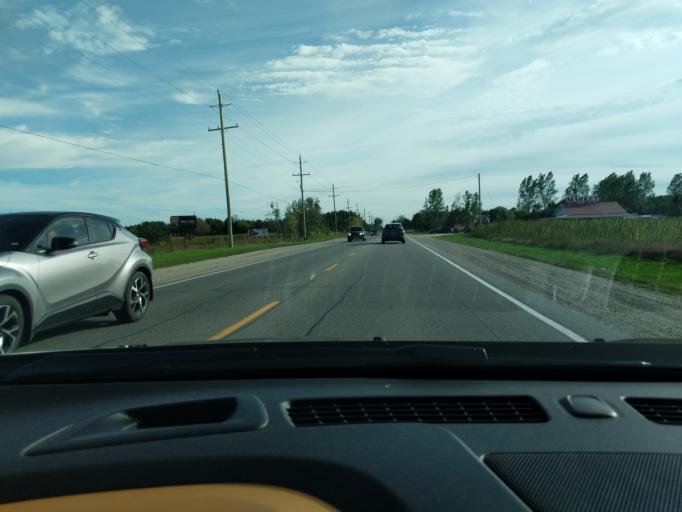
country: CA
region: Ontario
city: Wasaga Beach
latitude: 44.4411
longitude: -80.1011
